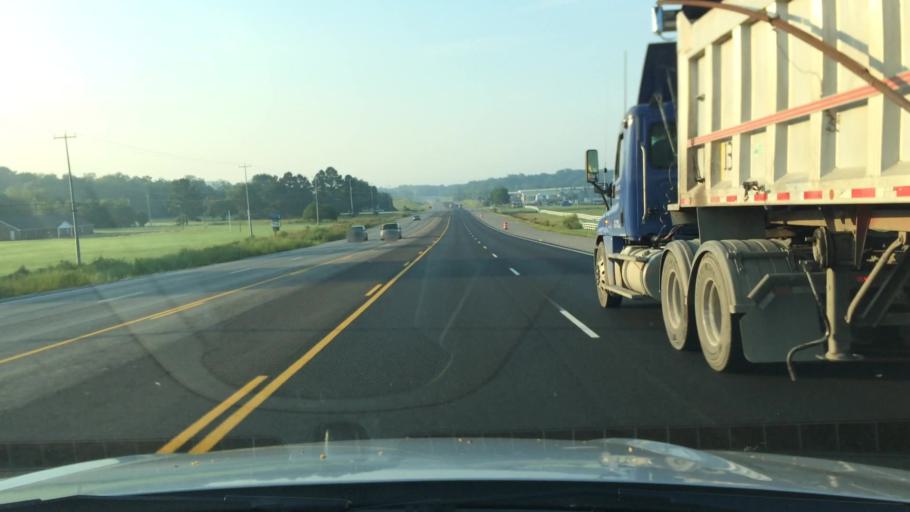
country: US
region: Tennessee
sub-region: Giles County
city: Pulaski
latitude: 35.1594
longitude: -87.0085
